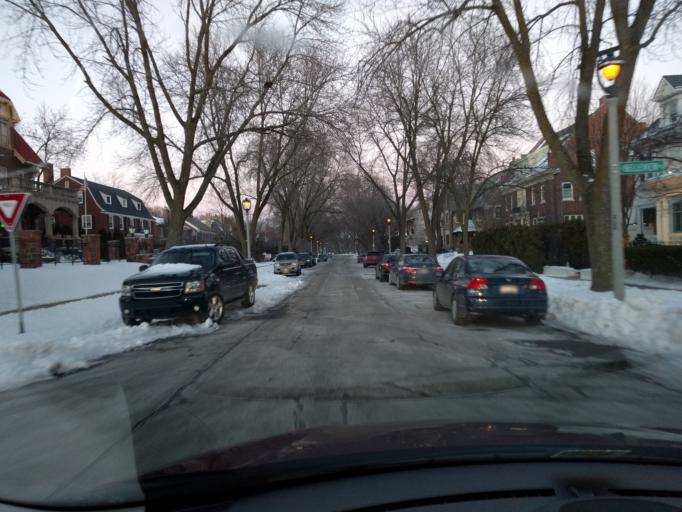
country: US
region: Wisconsin
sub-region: Milwaukee County
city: Shorewood
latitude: 43.0643
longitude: -87.8747
